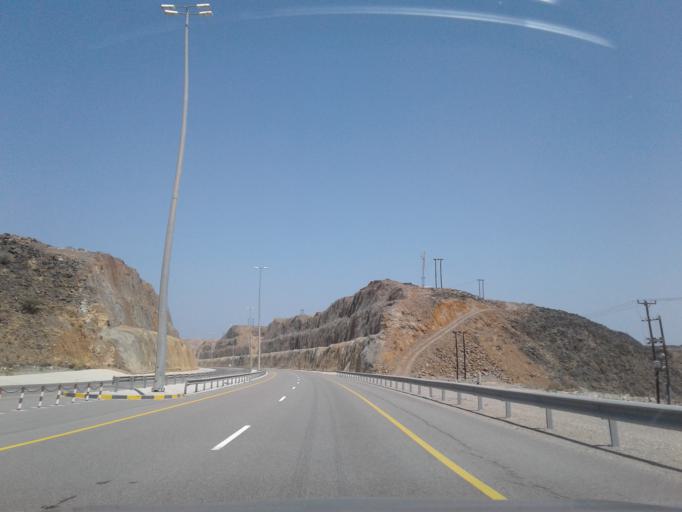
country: OM
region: Muhafazat Masqat
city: Muscat
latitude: 23.1883
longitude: 58.8586
